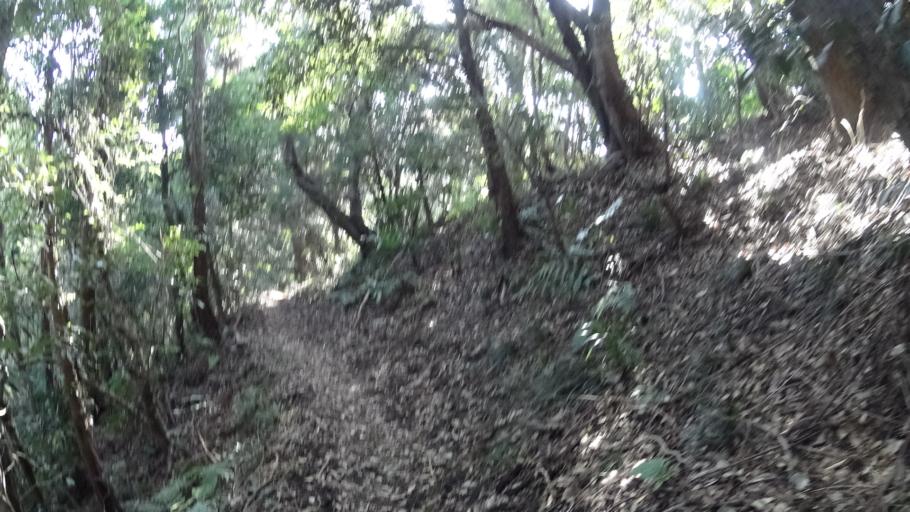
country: JP
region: Kanagawa
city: Zushi
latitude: 35.2903
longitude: 139.6222
